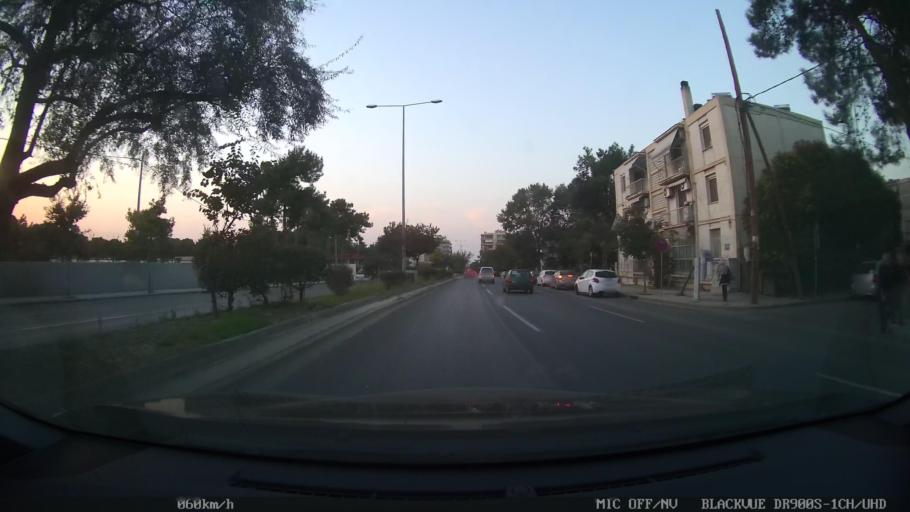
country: GR
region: Central Macedonia
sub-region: Nomos Thessalonikis
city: Kalamaria
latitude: 40.5801
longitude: 22.9673
